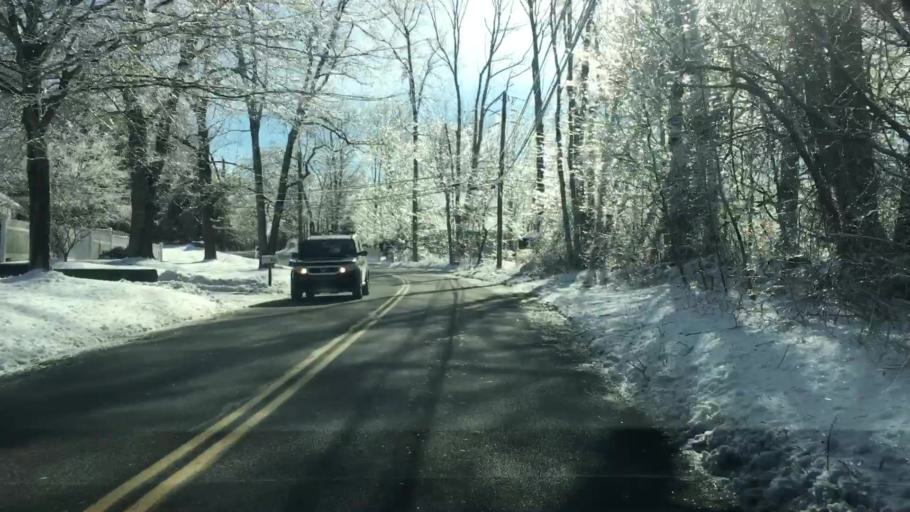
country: US
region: Connecticut
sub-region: Fairfield County
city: Trumbull
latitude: 41.3387
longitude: -73.2254
